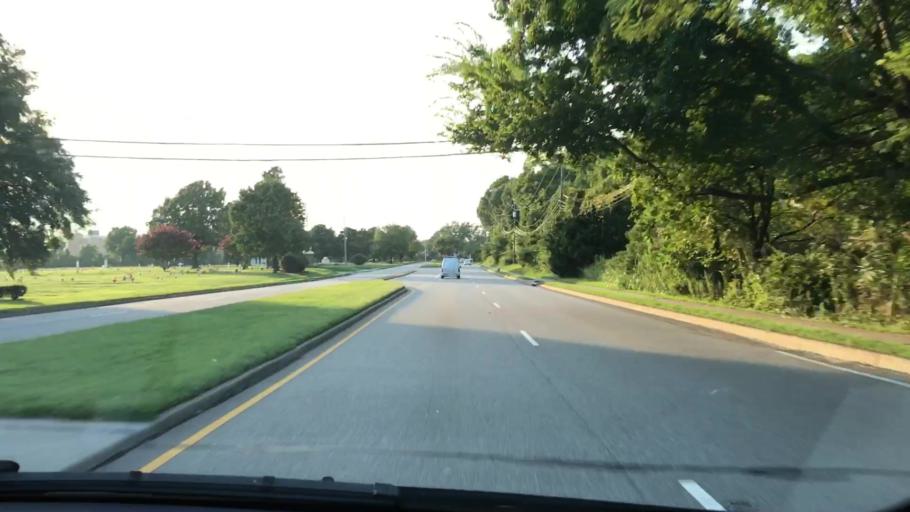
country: US
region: Virginia
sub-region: City of Hampton
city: Hampton
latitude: 37.0553
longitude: -76.3811
